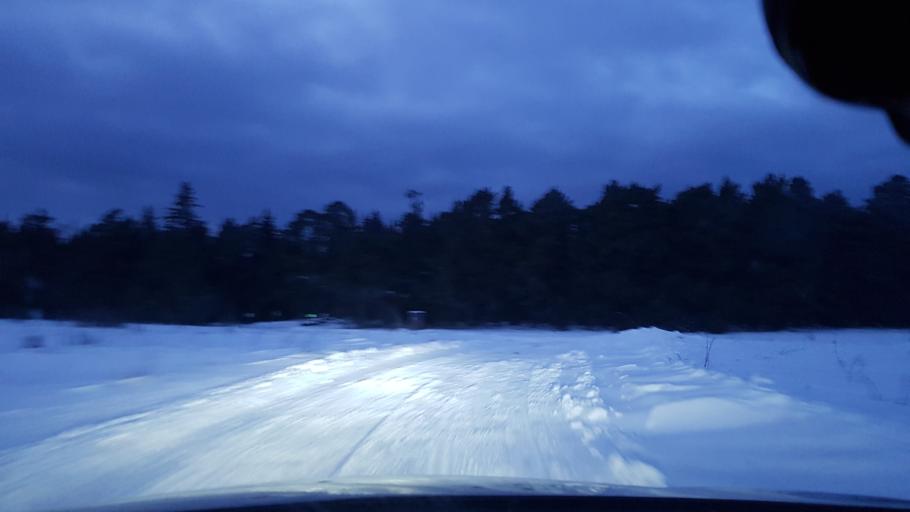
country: EE
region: Laeaene
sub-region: Haapsalu linn
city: Haapsalu
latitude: 59.2250
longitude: 23.5179
